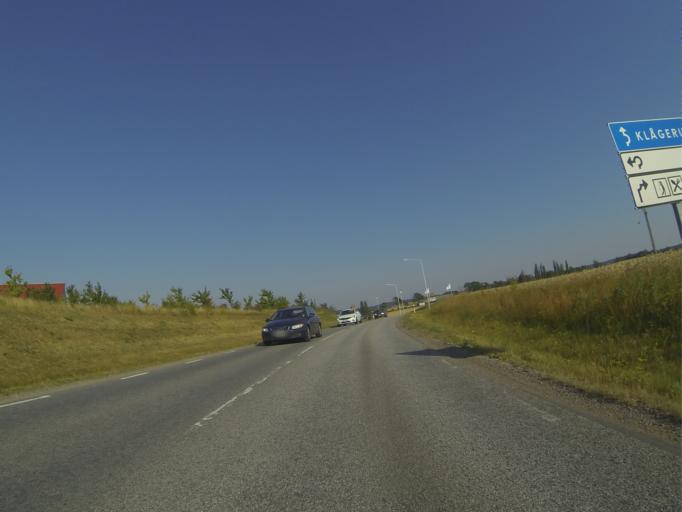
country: SE
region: Skane
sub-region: Staffanstorps Kommun
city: Staffanstorp
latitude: 55.5773
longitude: 13.1655
